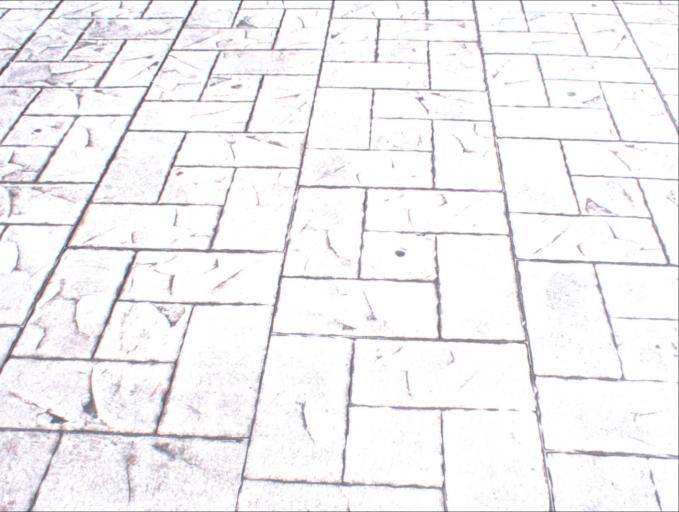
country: AU
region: Queensland
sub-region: Logan
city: Beenleigh
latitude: -27.7092
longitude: 153.1669
